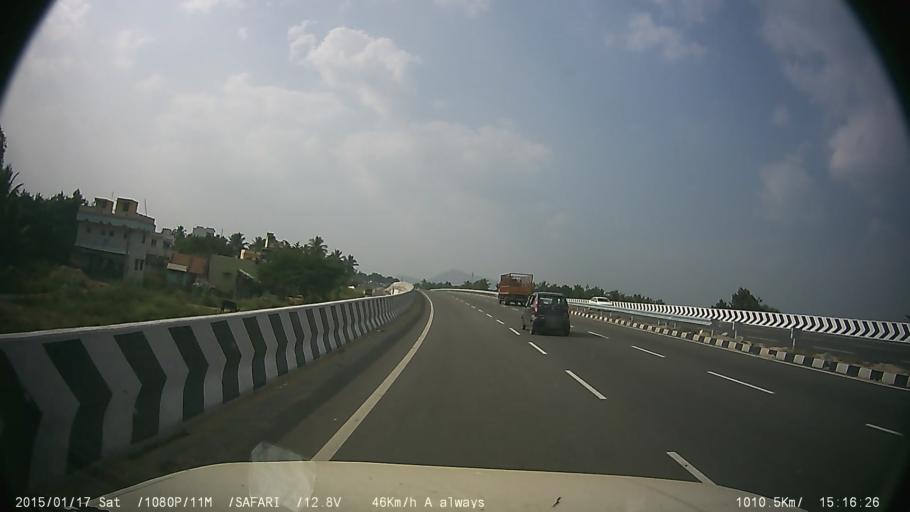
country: IN
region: Tamil Nadu
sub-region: Krishnagiri
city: Krishnagiri
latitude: 12.5747
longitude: 78.1684
